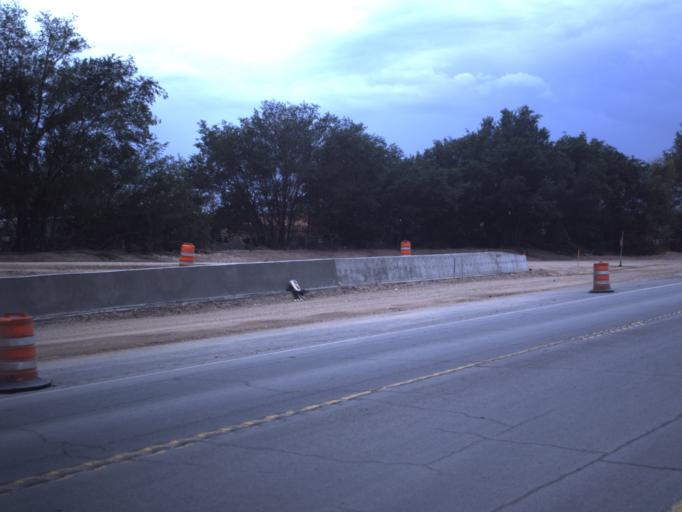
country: US
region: Utah
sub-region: Duchesne County
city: Roosevelt
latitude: 40.2472
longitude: -110.0675
